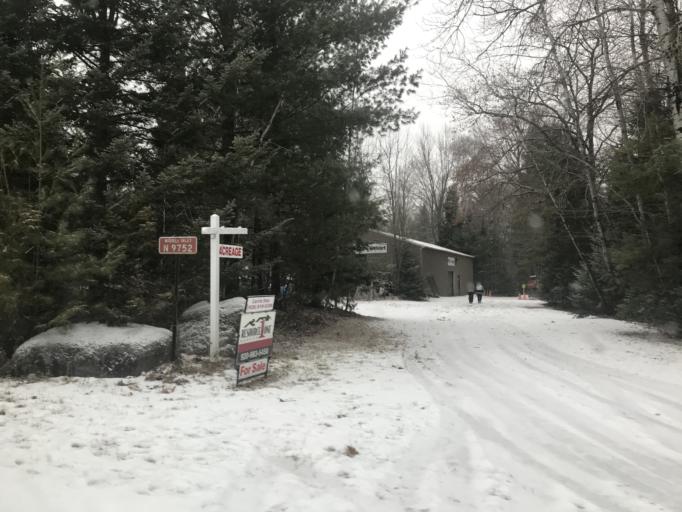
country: US
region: Wisconsin
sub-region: Marinette County
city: Peshtigo
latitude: 45.3082
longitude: -87.8796
